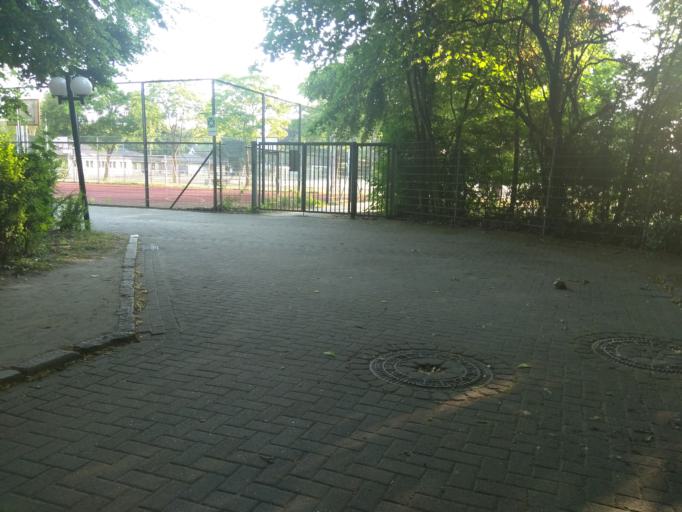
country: DE
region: Schleswig-Holstein
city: Grosshansdorf
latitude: 53.6480
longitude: 10.2776
